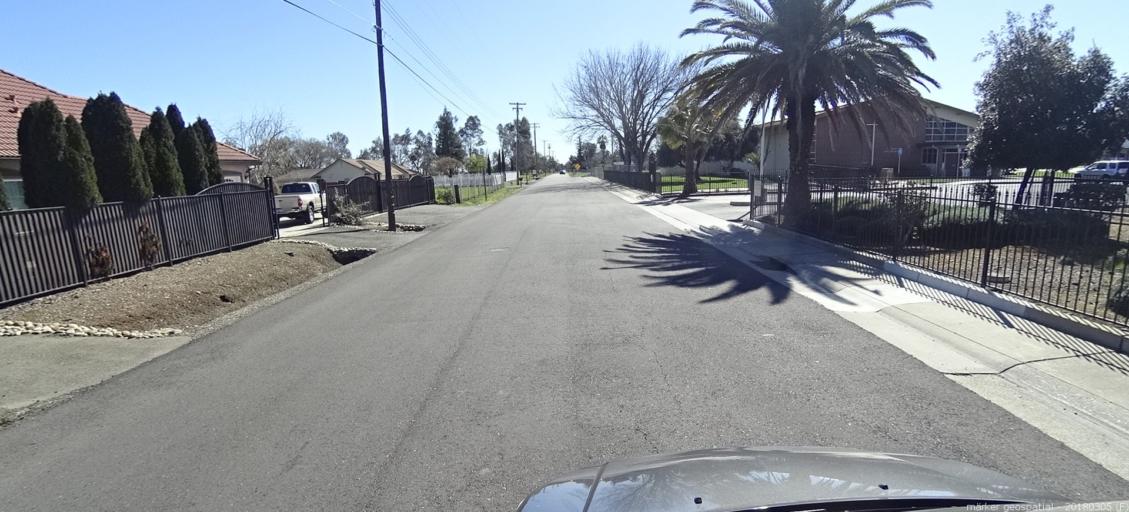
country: US
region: California
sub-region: Sacramento County
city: Florin
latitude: 38.4952
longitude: -121.3790
